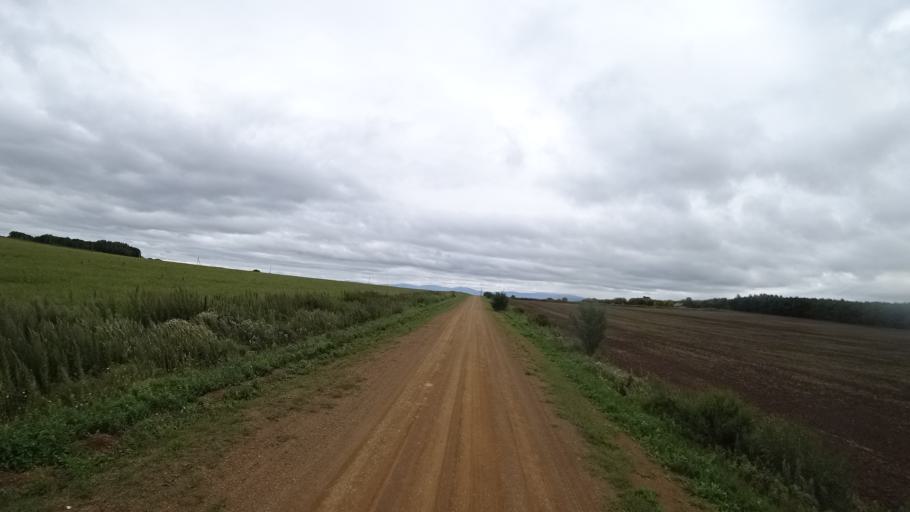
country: RU
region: Primorskiy
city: Chernigovka
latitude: 44.4357
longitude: 132.5884
